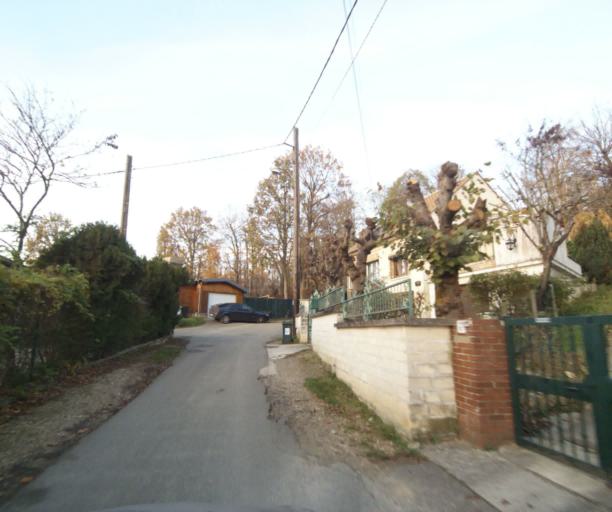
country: FR
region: Ile-de-France
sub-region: Departement des Yvelines
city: Triel-sur-Seine
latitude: 48.9846
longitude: 2.0116
